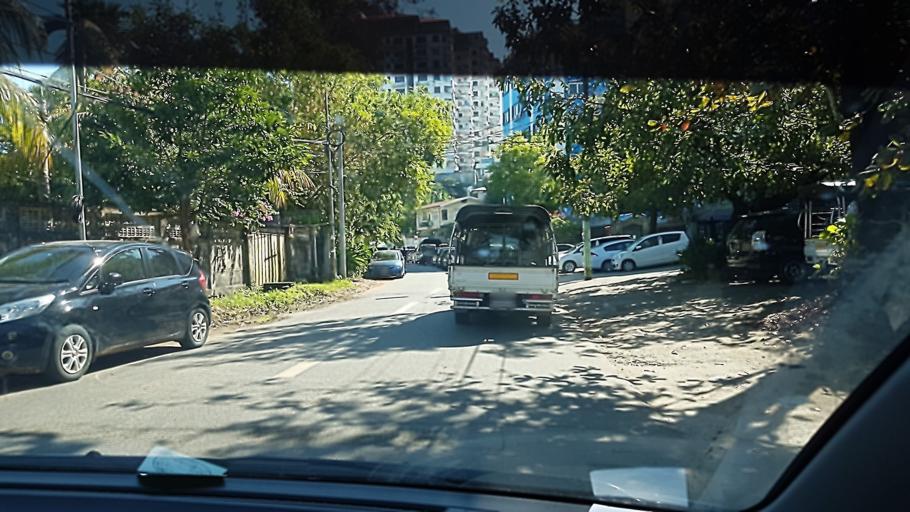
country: MM
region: Yangon
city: Yangon
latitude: 16.8176
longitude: 96.1548
